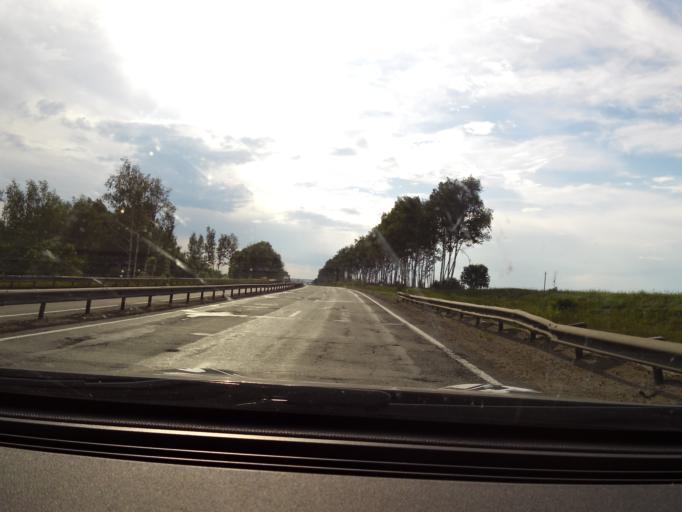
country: RU
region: Vladimir
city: Gorokhovets
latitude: 56.1649
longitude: 42.4903
